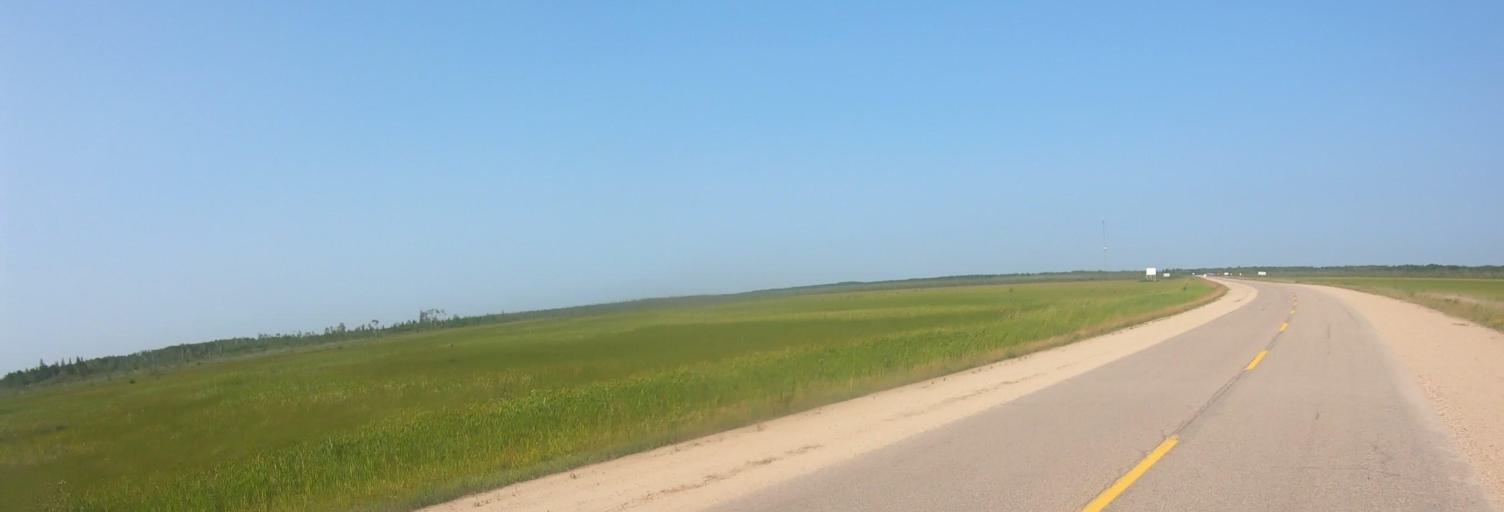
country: US
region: Minnesota
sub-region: Roseau County
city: Warroad
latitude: 49.0088
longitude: -95.3838
